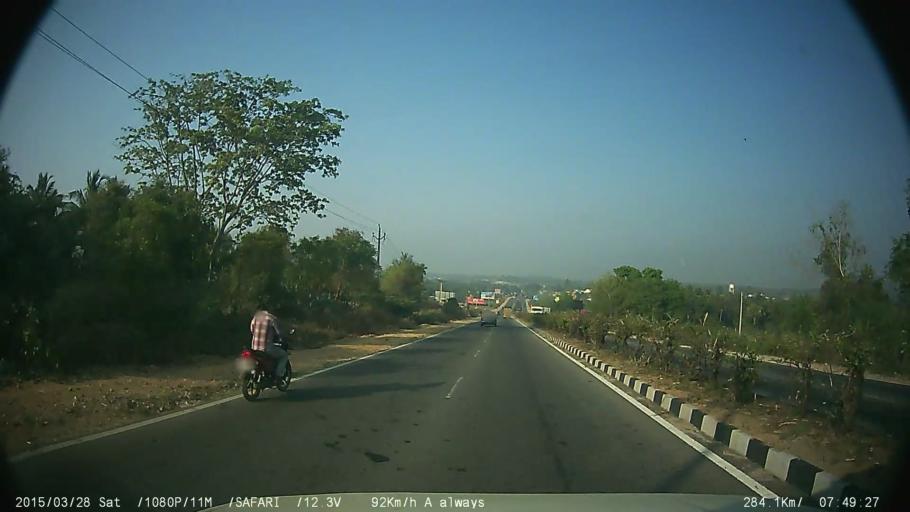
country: IN
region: Karnataka
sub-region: Mandya
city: Pandavapura
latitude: 12.4720
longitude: 76.7598
